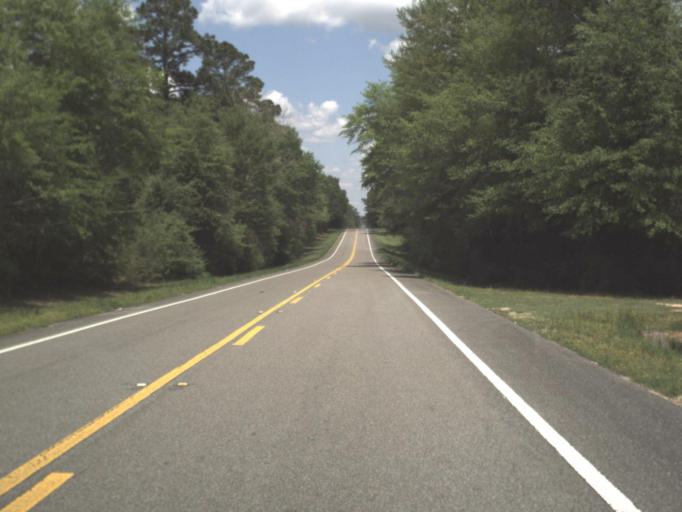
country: US
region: Florida
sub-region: Okaloosa County
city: Crestview
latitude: 30.9616
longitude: -86.6324
